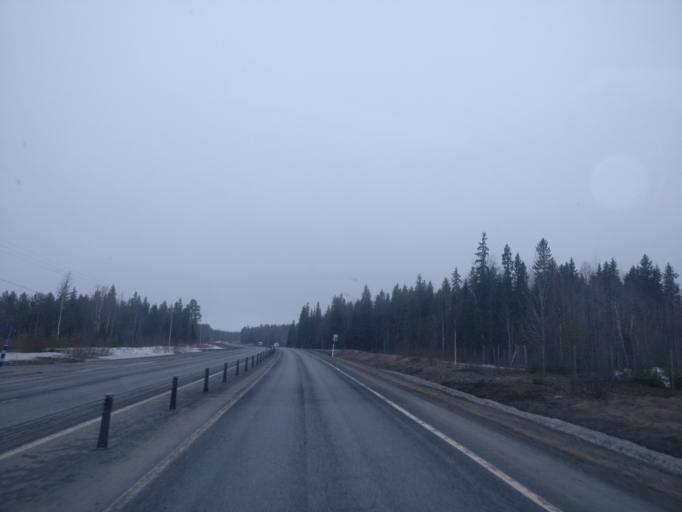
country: FI
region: Lapland
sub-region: Kemi-Tornio
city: Simo
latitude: 65.6689
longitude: 24.9579
